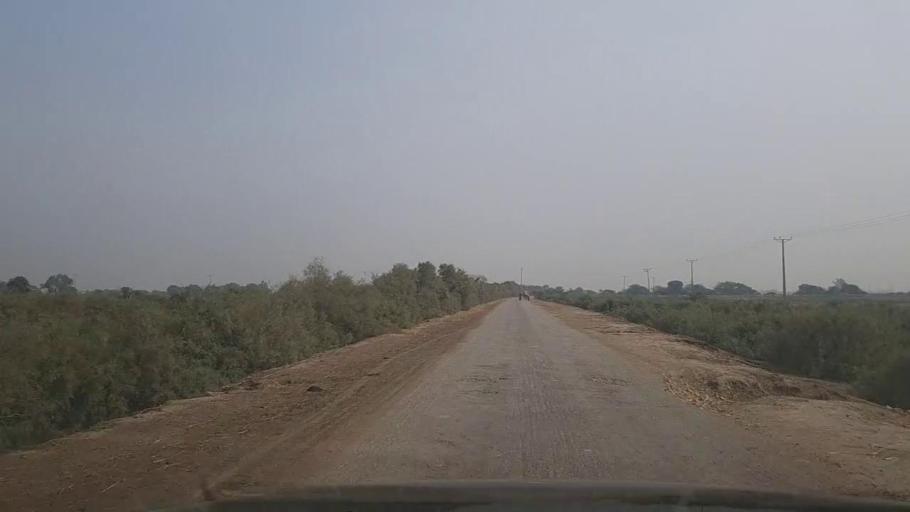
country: PK
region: Sindh
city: Mirpur Sakro
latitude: 24.4787
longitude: 67.6564
